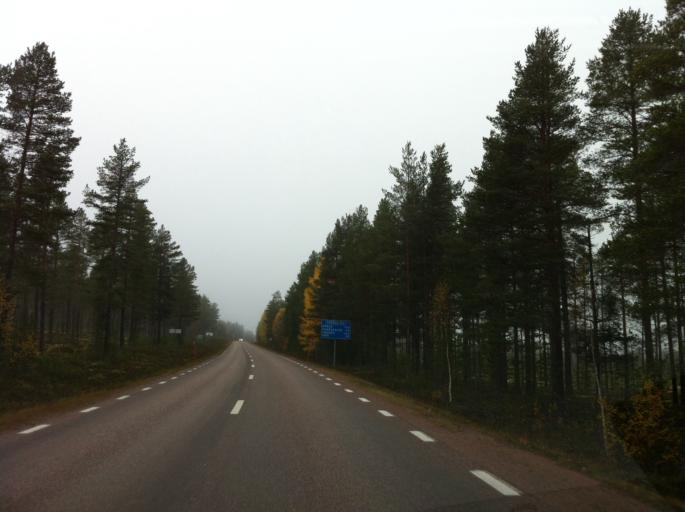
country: NO
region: Hedmark
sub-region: Trysil
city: Innbygda
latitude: 61.6949
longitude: 13.1162
